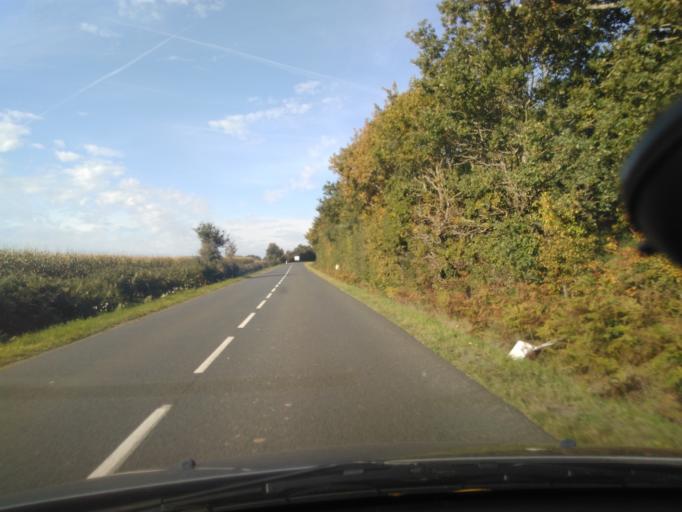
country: FR
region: Pays de la Loire
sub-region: Departement de la Vendee
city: Saint-Hilaire-de-Talmont
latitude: 46.4906
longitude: -1.5845
